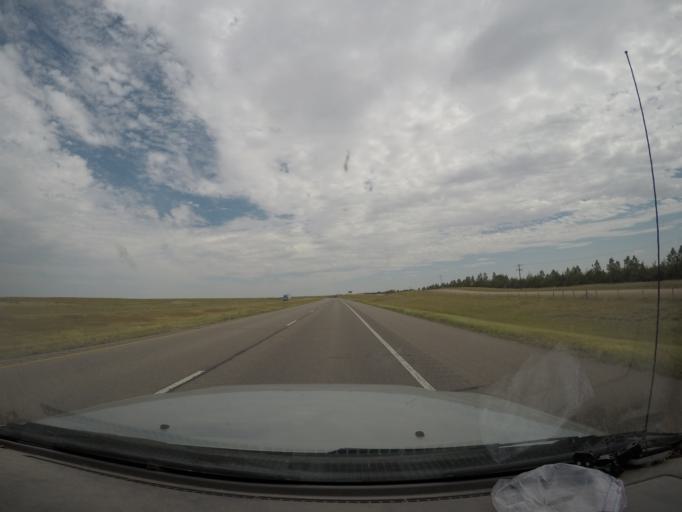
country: US
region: Nebraska
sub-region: Kimball County
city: Kimball
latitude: 41.1920
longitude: -103.7769
